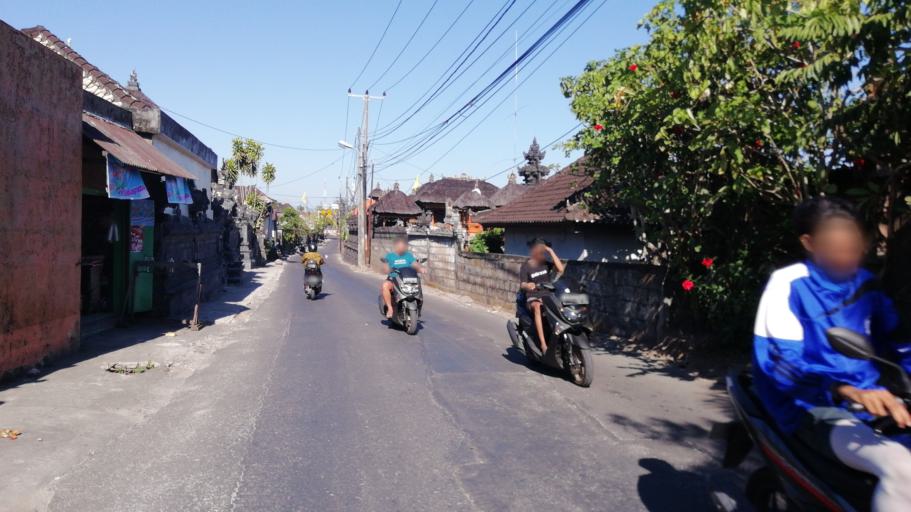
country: ID
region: Bali
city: Jimbaran
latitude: -8.8271
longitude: 115.1661
